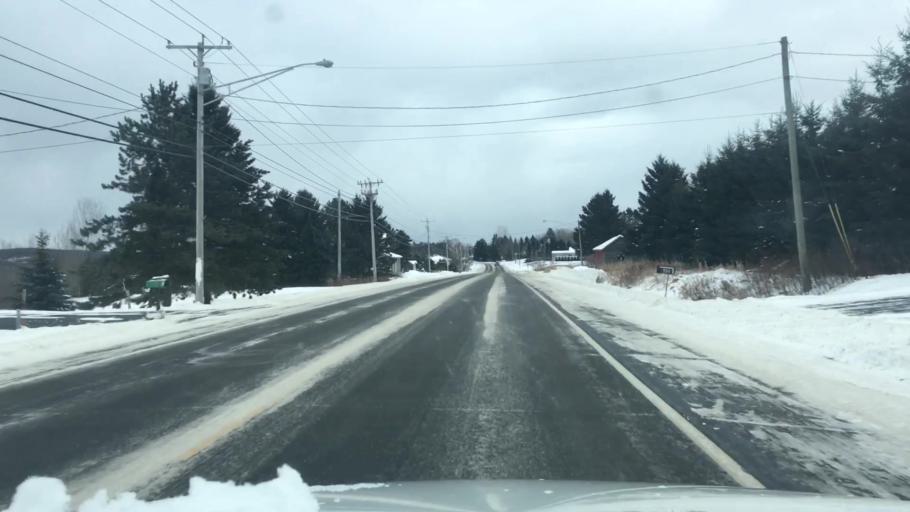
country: US
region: Maine
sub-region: Aroostook County
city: Madawaska
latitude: 47.3475
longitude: -68.2699
